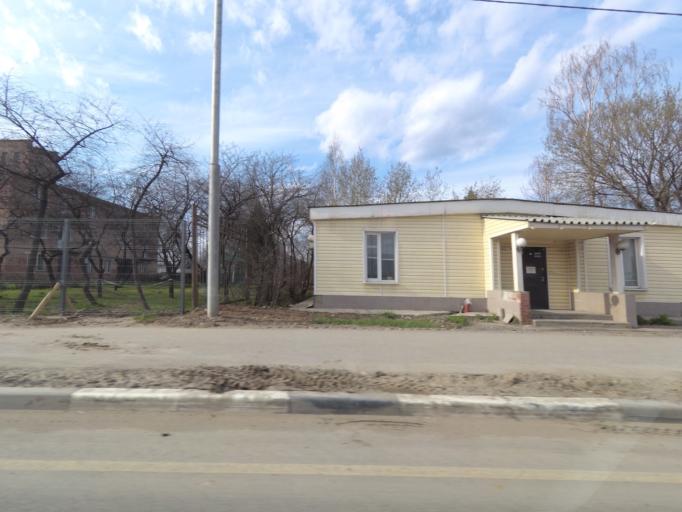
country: RU
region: Moskovskaya
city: Lobnya
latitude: 55.9837
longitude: 37.4414
